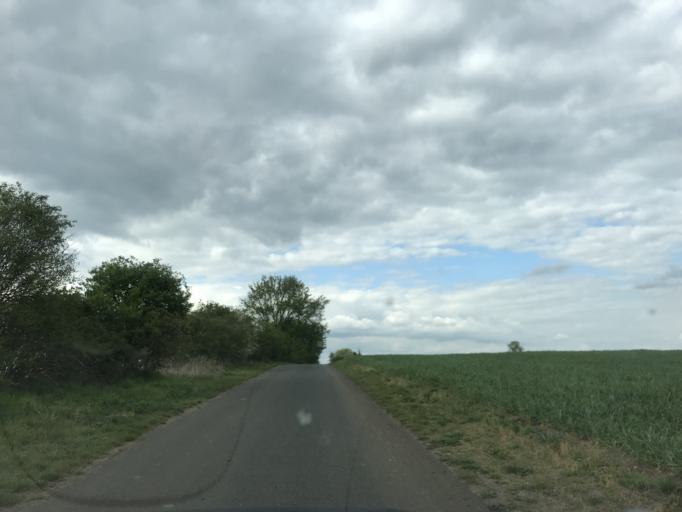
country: PL
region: West Pomeranian Voivodeship
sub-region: Powiat mysliborski
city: Mysliborz
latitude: 52.8757
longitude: 14.8925
